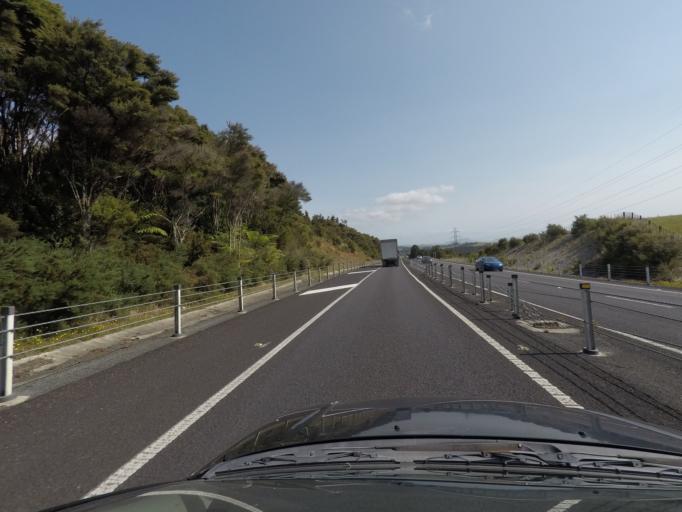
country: NZ
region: Northland
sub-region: Whangarei
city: Ruakaka
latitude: -36.0422
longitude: 174.4179
